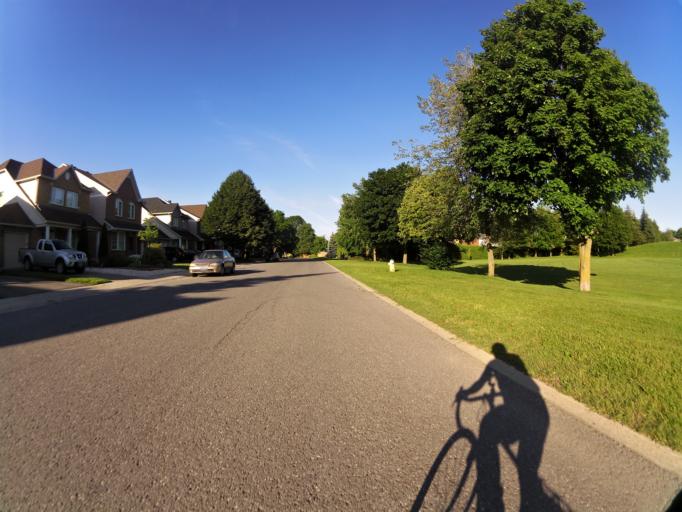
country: CA
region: Ontario
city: Bells Corners
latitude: 45.3329
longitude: -75.7667
